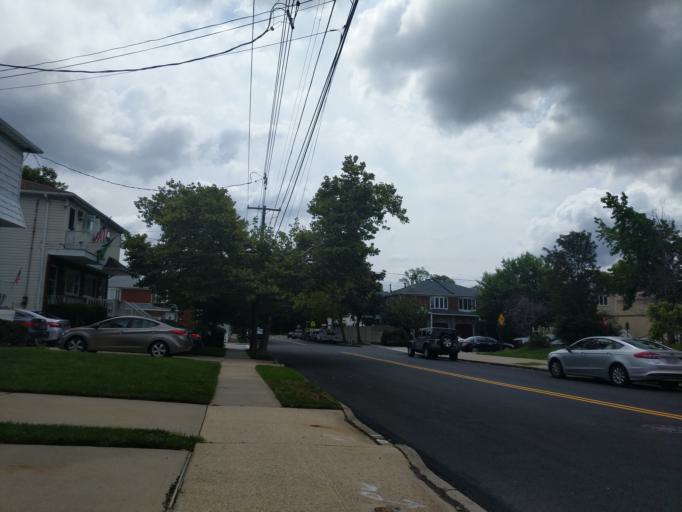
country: US
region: New York
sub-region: Richmond County
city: Staten Island
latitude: 40.5522
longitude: -74.1356
